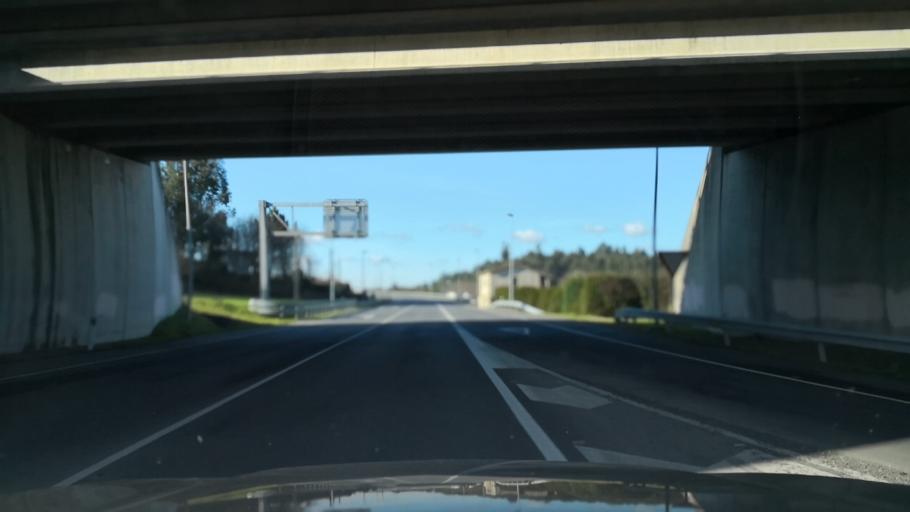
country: ES
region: Galicia
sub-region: Provincia de Pontevedra
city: Silleda
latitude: 42.7193
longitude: -8.2842
